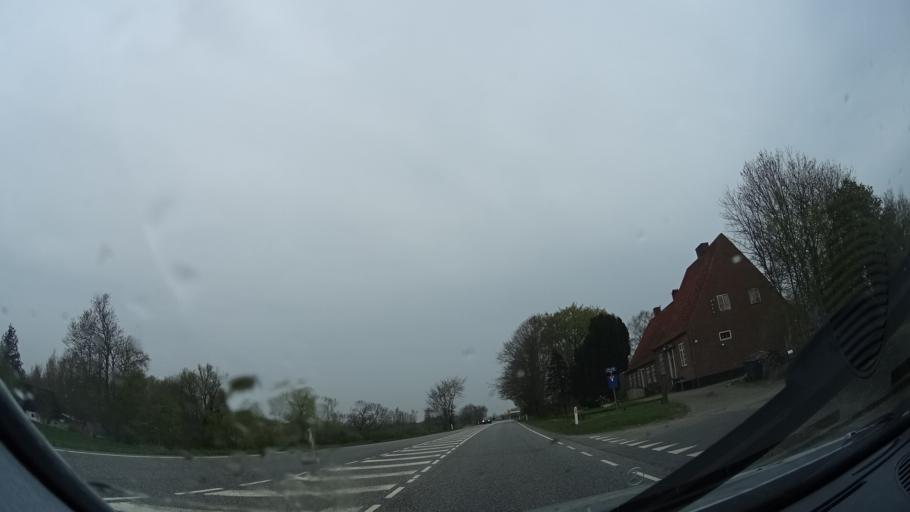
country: DK
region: Zealand
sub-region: Odsherred Kommune
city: Asnaes
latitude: 55.7922
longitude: 11.5996
